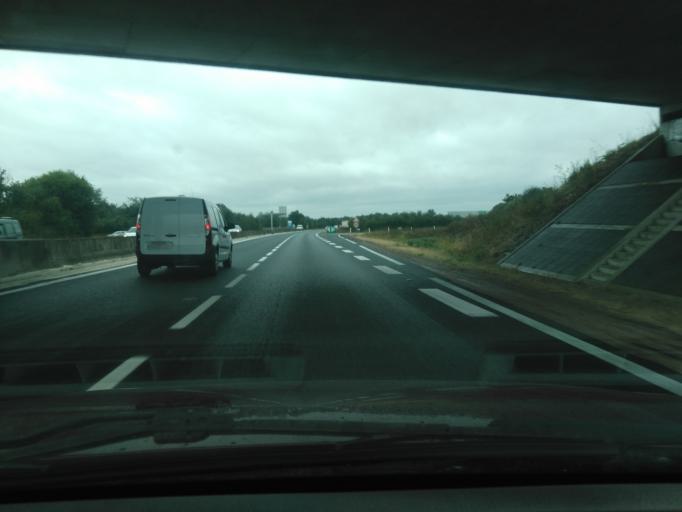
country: FR
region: Pays de la Loire
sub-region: Departement de la Vendee
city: La Chaize-le-Vicomte
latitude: 46.6669
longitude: -1.3427
